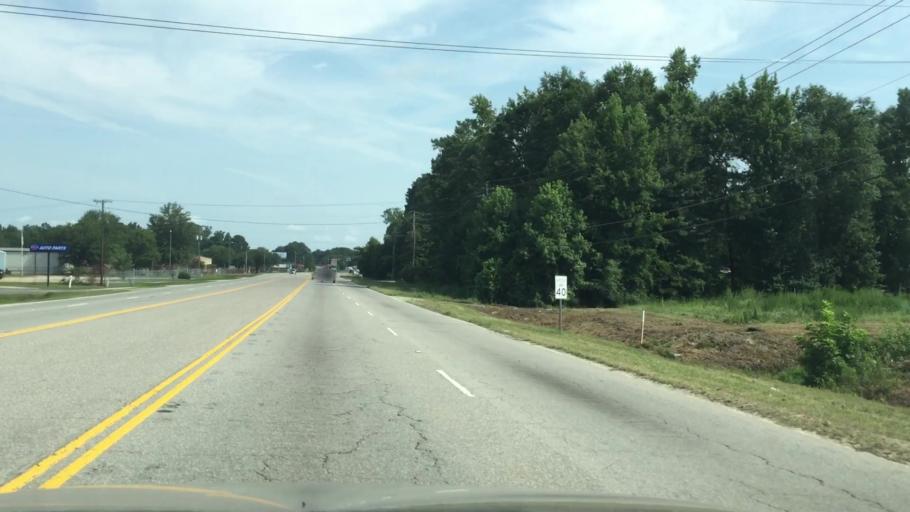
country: US
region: South Carolina
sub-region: Sumter County
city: South Sumter
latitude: 33.8969
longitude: -80.3528
